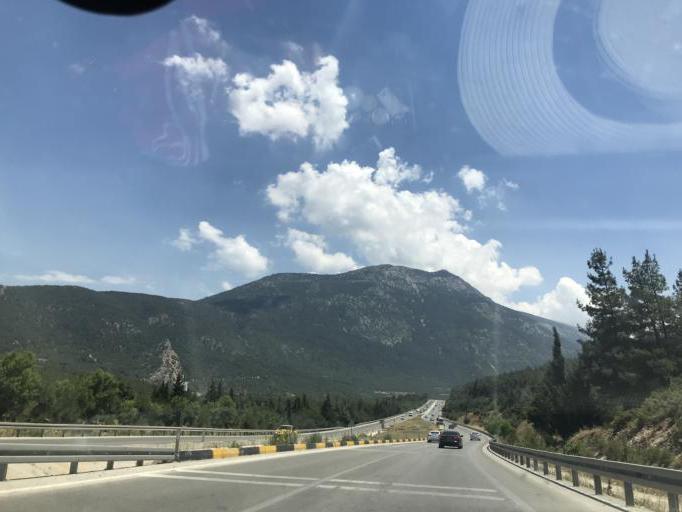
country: TR
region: Denizli
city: Honaz
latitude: 37.7296
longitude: 29.1943
